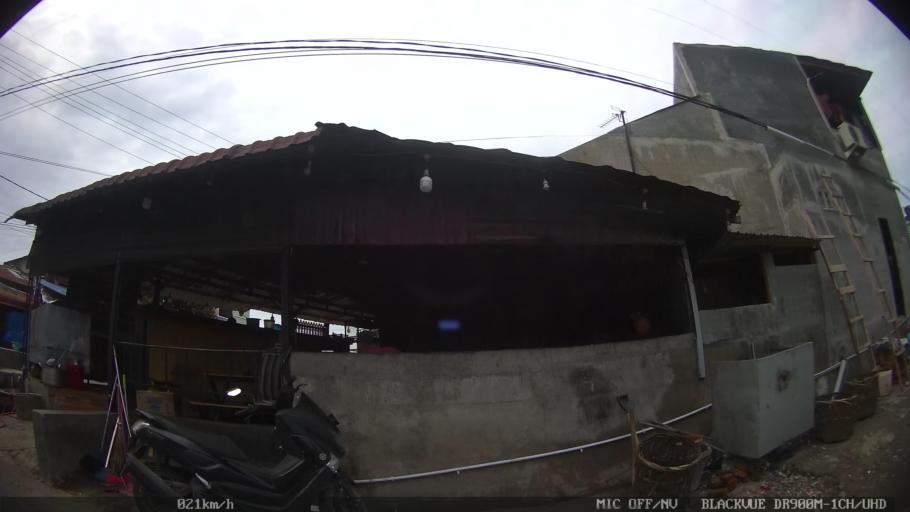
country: ID
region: North Sumatra
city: Sunggal
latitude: 3.5730
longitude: 98.5845
